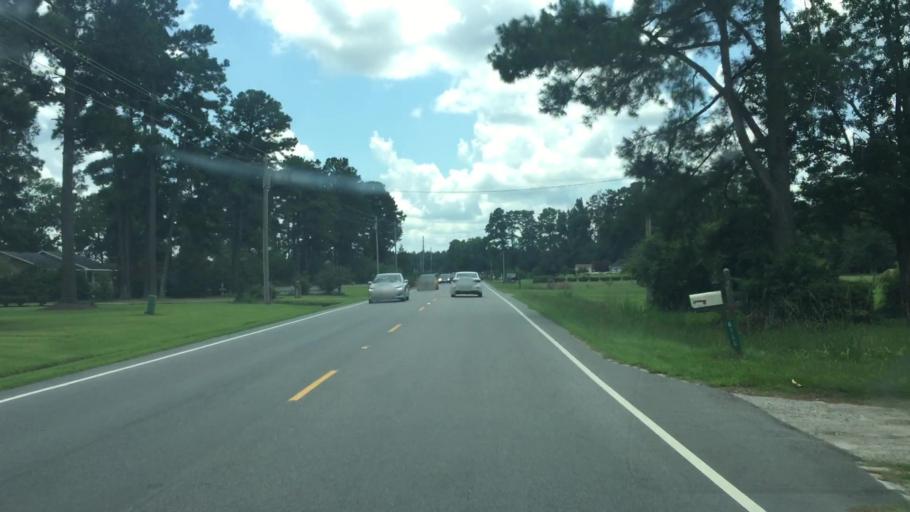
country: US
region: North Carolina
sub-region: Columbus County
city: Chadbourn
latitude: 34.2381
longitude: -78.8229
